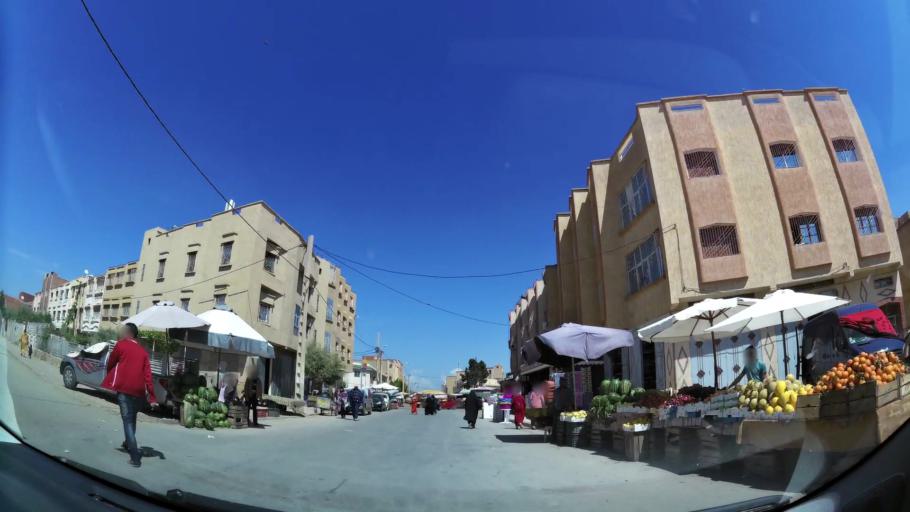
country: MA
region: Oriental
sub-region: Oujda-Angad
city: Oujda
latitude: 34.6861
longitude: -1.9327
